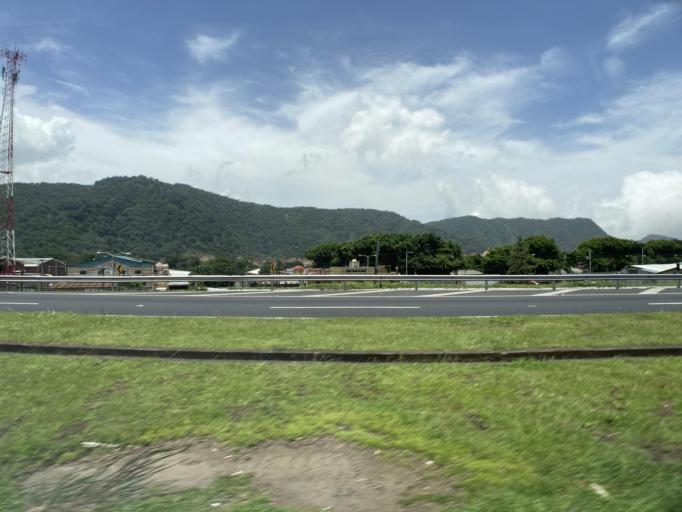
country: GT
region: Escuintla
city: Palin
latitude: 14.4108
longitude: -90.6833
